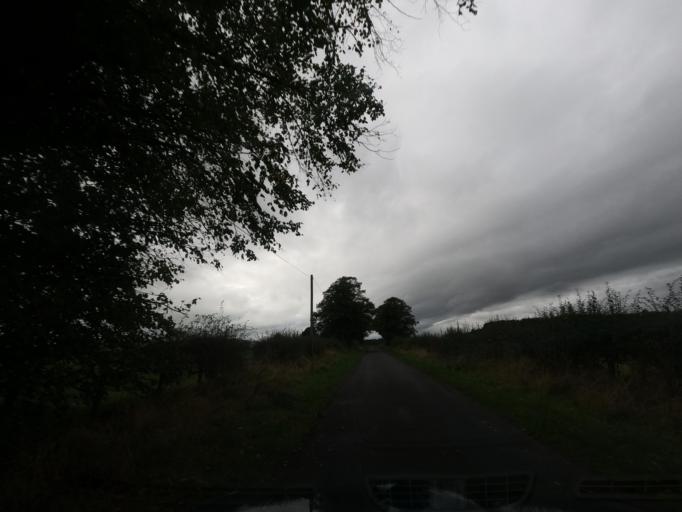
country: GB
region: England
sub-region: Northumberland
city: Doddington
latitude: 55.6010
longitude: -2.0340
